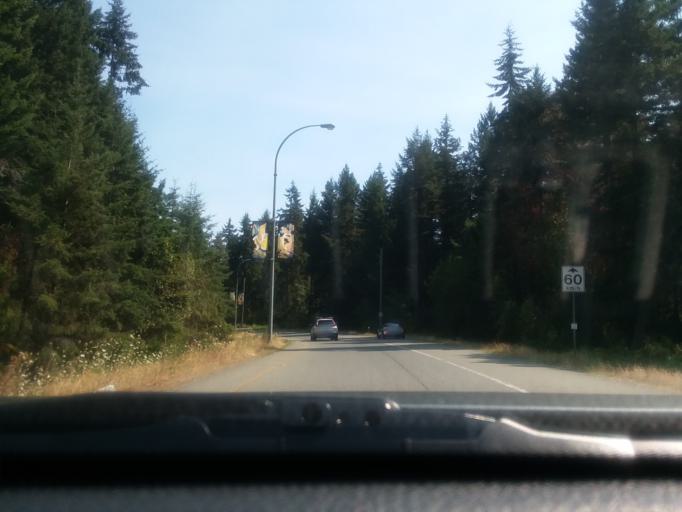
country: CA
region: British Columbia
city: Nanaimo
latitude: 49.2414
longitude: -124.0642
